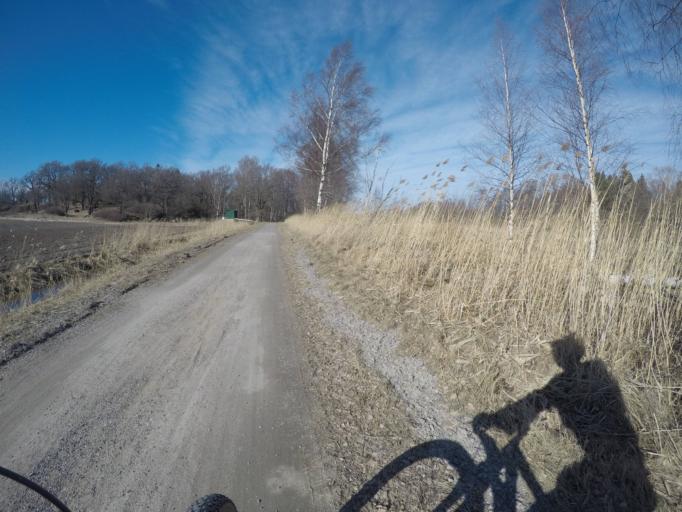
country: SE
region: Soedermanland
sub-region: Eskilstuna Kommun
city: Torshalla
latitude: 59.4085
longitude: 16.4647
